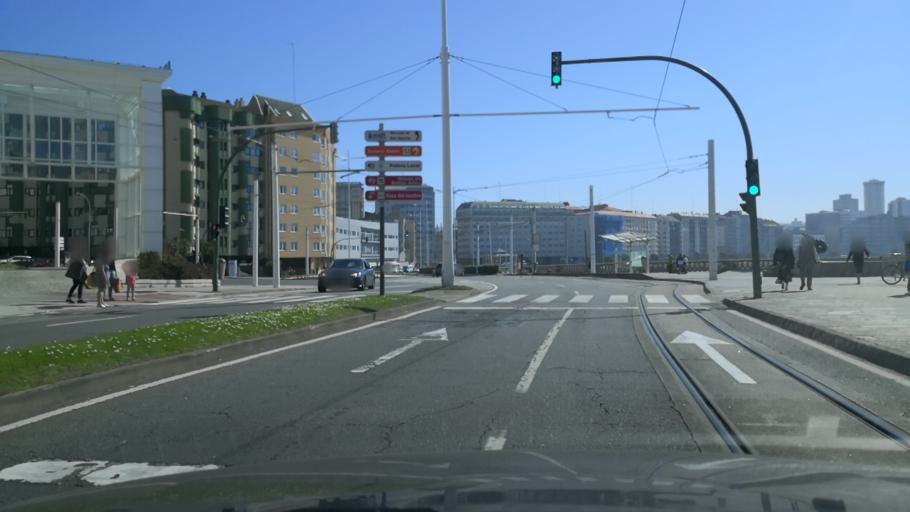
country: ES
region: Galicia
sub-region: Provincia da Coruna
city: A Coruna
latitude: 43.3755
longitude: -8.4033
